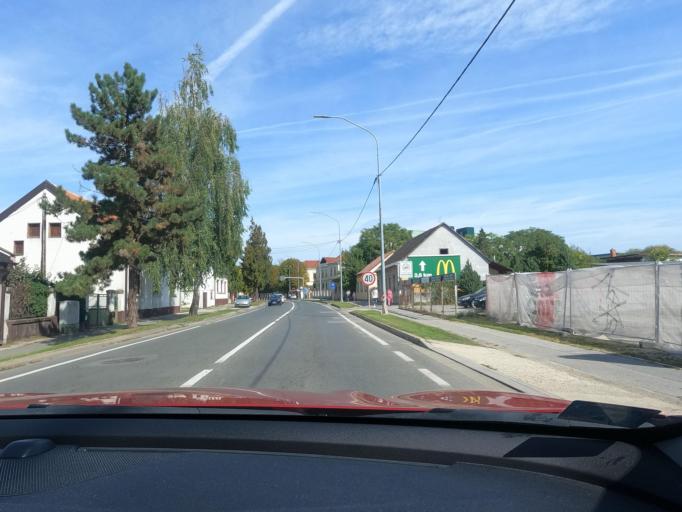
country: HR
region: Sisacko-Moslavacka
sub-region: Grad Sisak
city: Sisak
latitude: 45.4752
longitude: 16.3677
